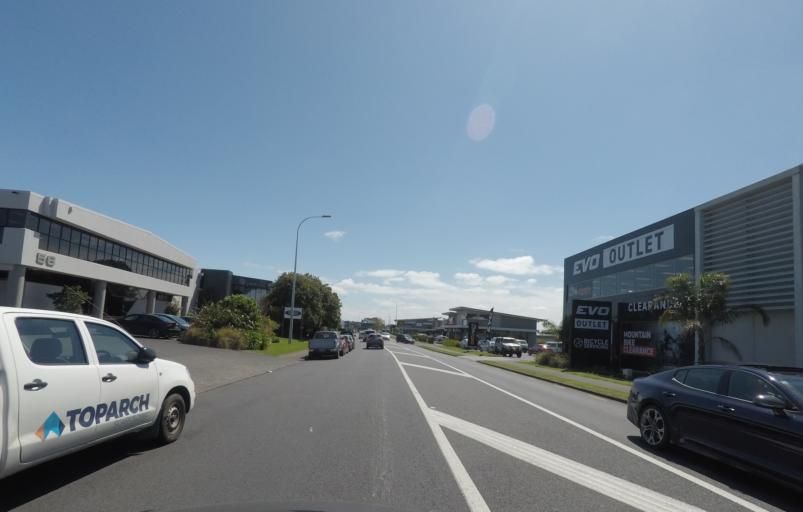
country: NZ
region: Auckland
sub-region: Auckland
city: Tamaki
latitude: -36.8920
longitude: 174.8364
